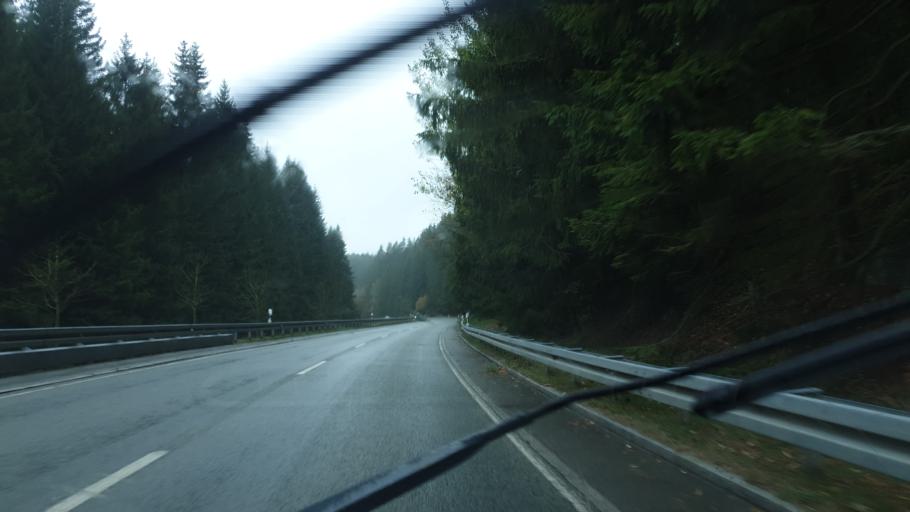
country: DE
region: Saxony
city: Muldenhammer
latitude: 50.4573
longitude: 12.4860
